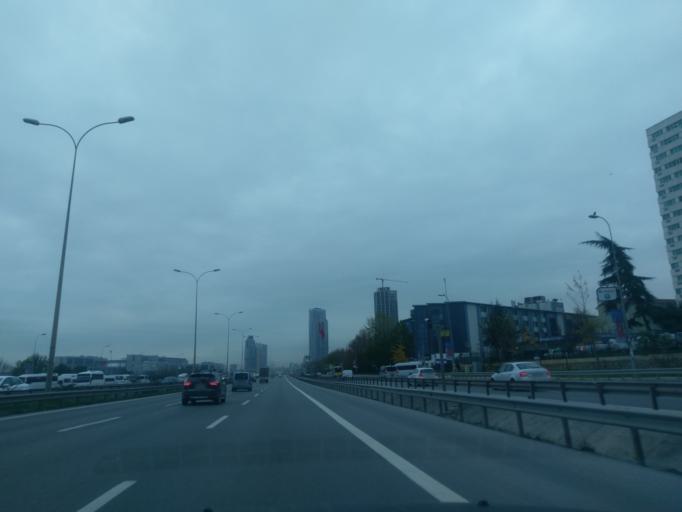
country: TR
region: Istanbul
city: Maltepe
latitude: 40.9137
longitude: 29.1887
